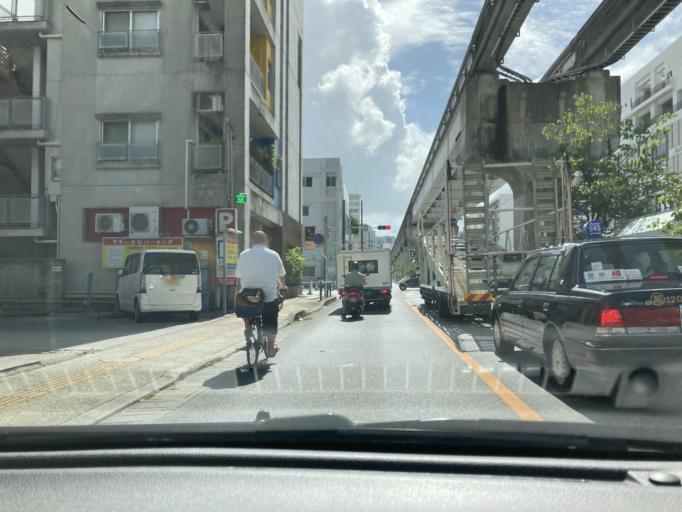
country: JP
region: Okinawa
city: Naha-shi
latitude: 26.2175
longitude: 127.6824
